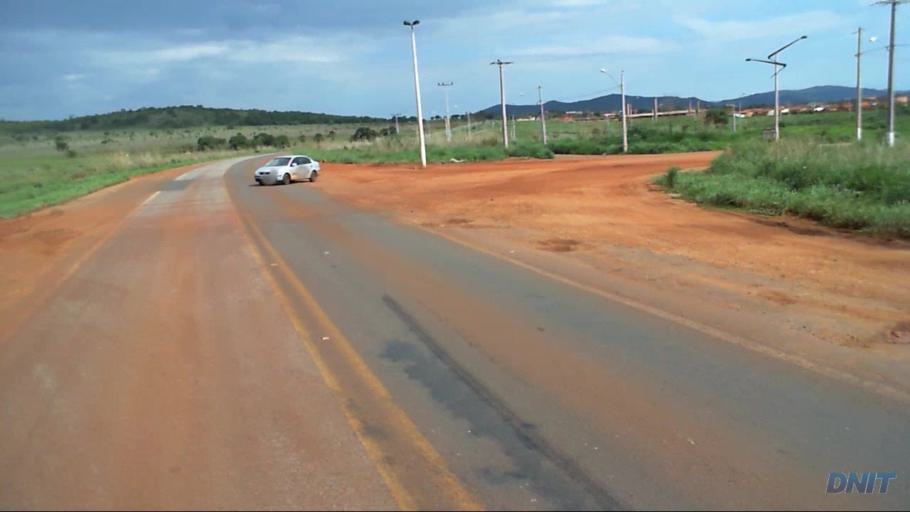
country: BR
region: Goias
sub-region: Barro Alto
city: Barro Alto
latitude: -14.9815
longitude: -48.9282
